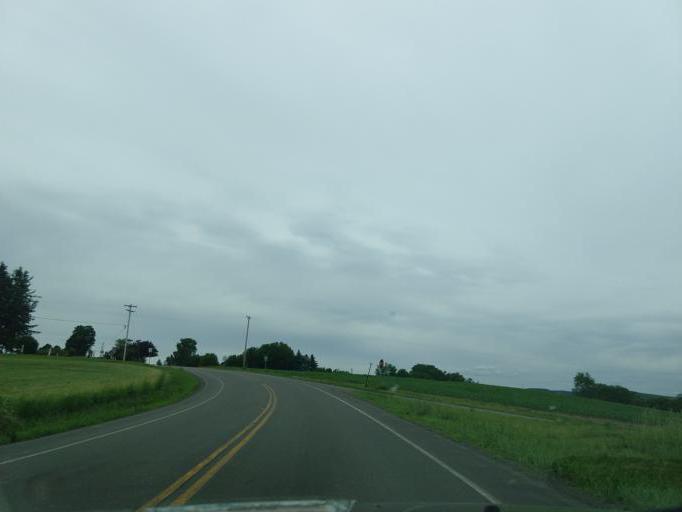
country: US
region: New York
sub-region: Cortland County
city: Munsons Corners
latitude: 42.5055
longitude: -76.1969
